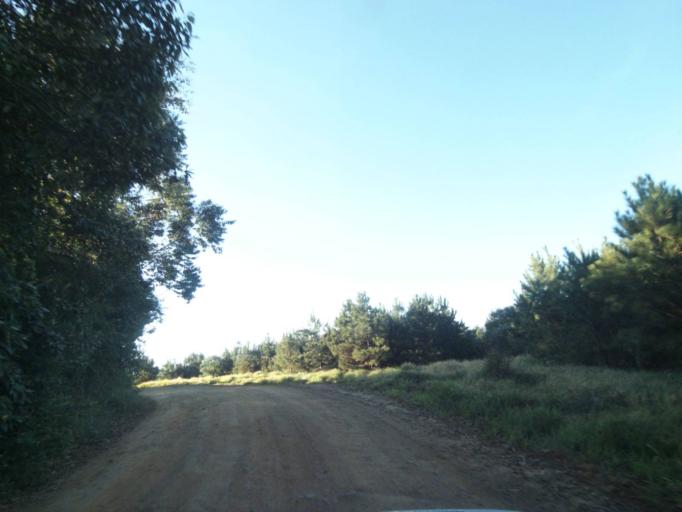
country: BR
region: Parana
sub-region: Tibagi
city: Tibagi
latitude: -24.5247
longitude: -50.5922
